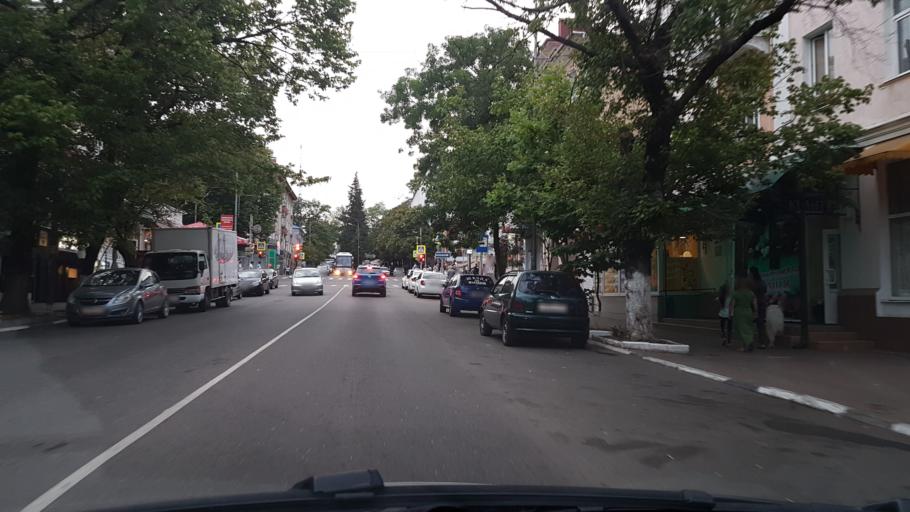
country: RU
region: Krasnodarskiy
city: Tuapse
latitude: 44.0968
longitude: 39.0770
